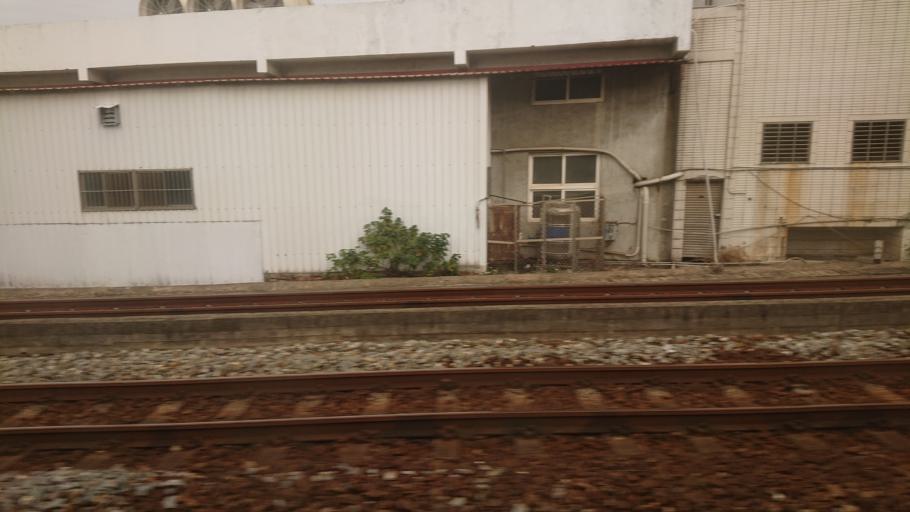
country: TW
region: Taiwan
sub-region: Changhua
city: Chang-hua
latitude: 24.0970
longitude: 120.5696
